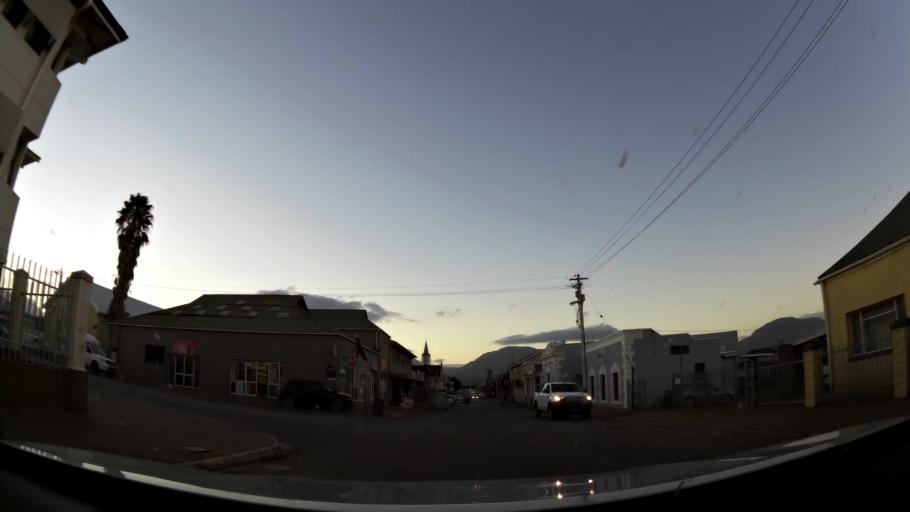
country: ZA
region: Western Cape
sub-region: Eden District Municipality
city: Riversdale
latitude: -34.0934
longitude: 21.2618
